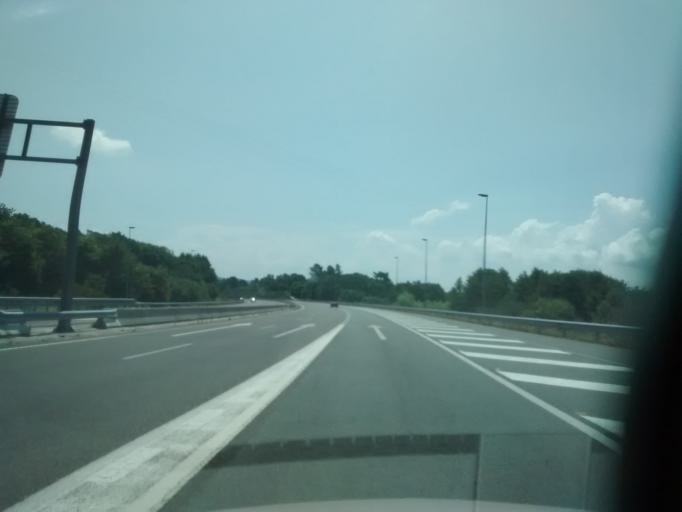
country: ES
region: Galicia
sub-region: Provincia de Ourense
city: Maside
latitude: 42.4052
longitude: -8.0106
